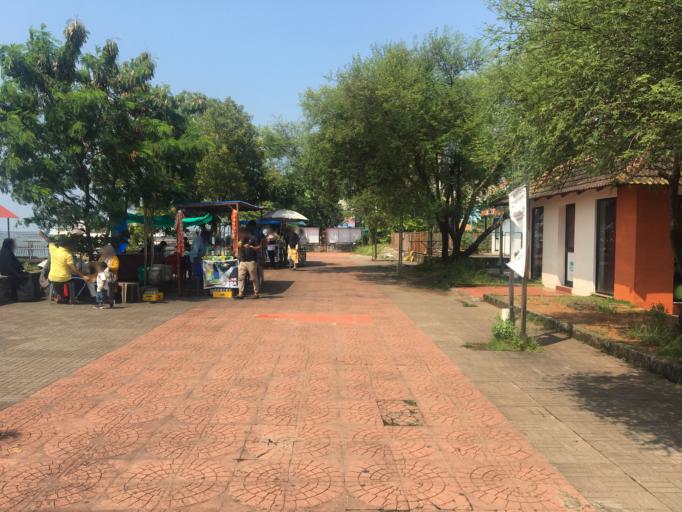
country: IN
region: Kerala
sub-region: Ernakulam
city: Cochin
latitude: 9.9730
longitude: 76.2783
